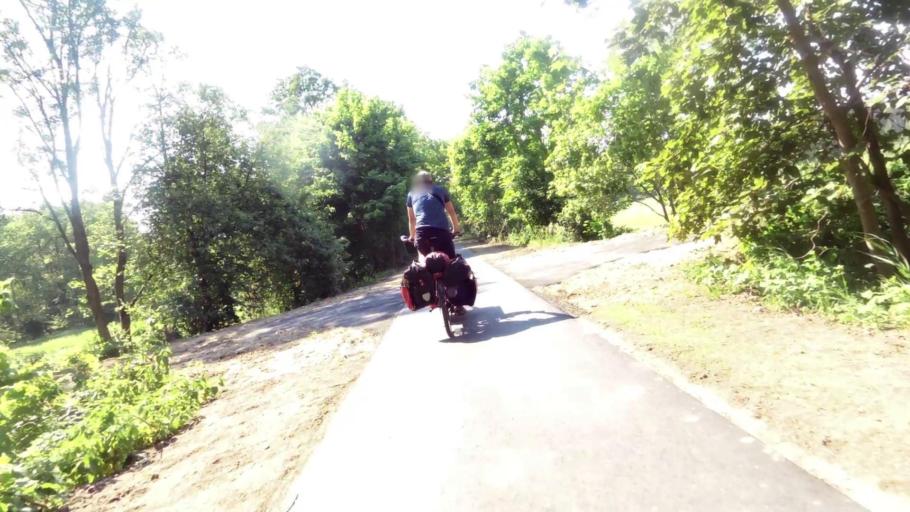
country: PL
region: West Pomeranian Voivodeship
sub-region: Powiat gryfinski
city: Gryfino
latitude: 53.2239
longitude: 14.5507
